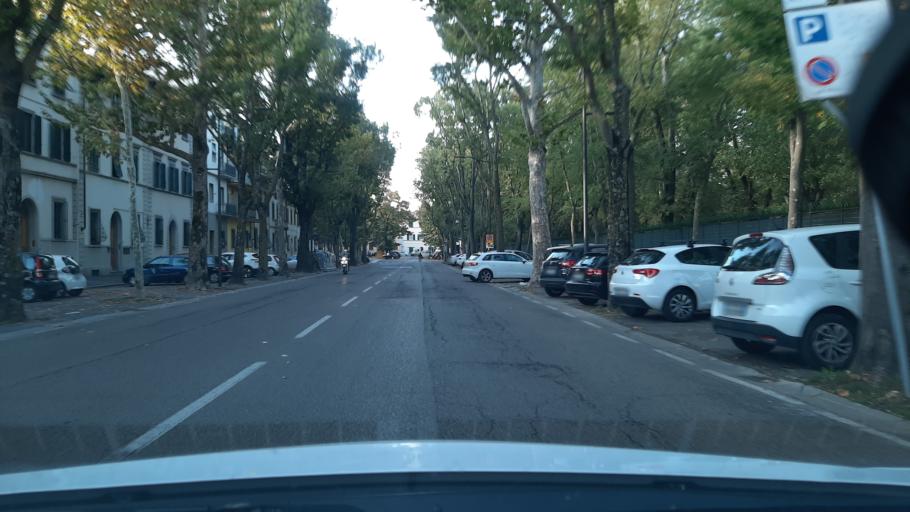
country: IT
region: Tuscany
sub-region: Province of Florence
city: Fiesole
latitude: 43.7758
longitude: 11.2853
